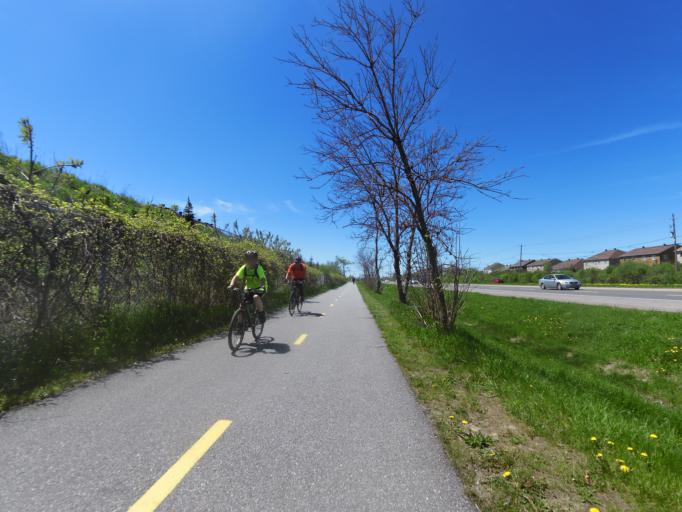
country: CA
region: Ontario
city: Bells Corners
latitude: 45.4097
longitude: -75.8463
